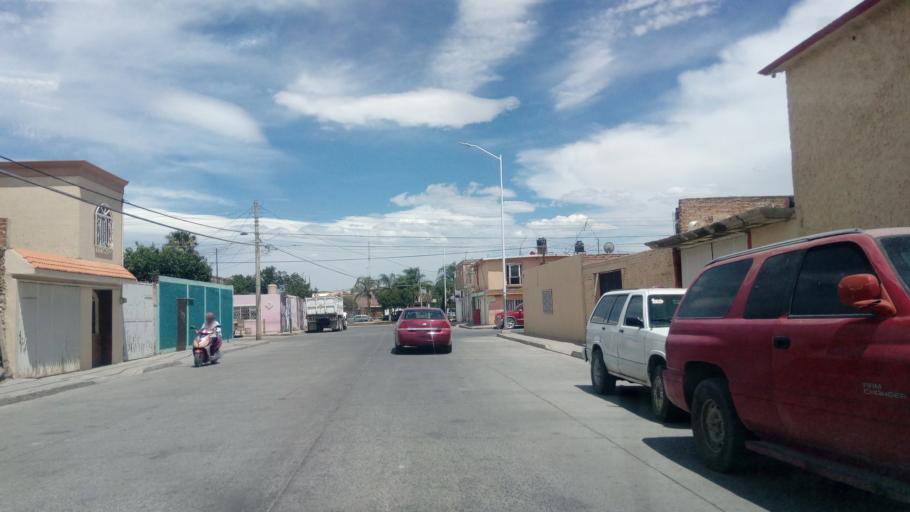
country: MX
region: Durango
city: Victoria de Durango
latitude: 23.9939
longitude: -104.6749
